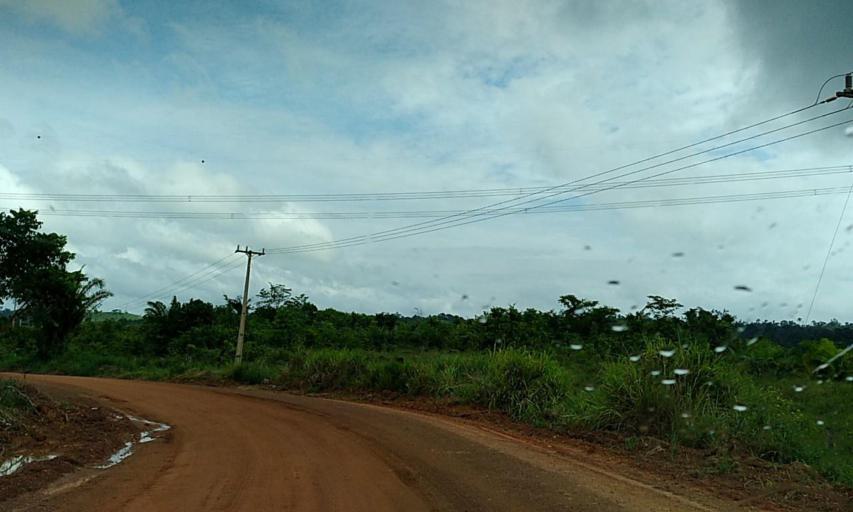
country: BR
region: Para
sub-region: Altamira
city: Altamira
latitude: -3.0924
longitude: -51.6328
